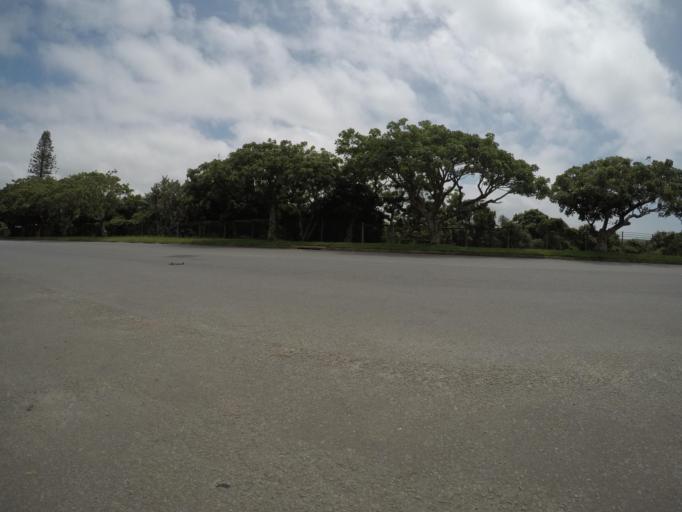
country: ZA
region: Eastern Cape
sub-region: Buffalo City Metropolitan Municipality
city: East London
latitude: -32.9400
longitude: 28.0178
